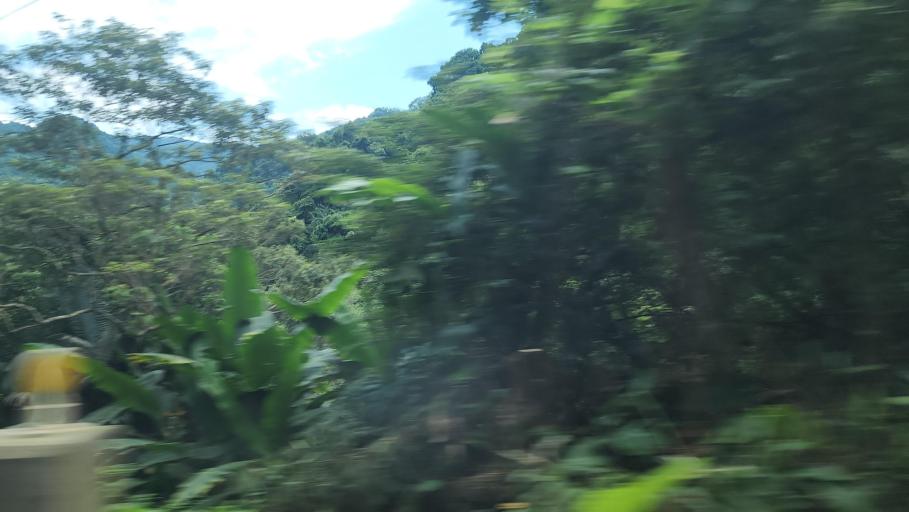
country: TW
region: Taipei
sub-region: Taipei
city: Banqiao
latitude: 24.9003
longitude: 121.4303
